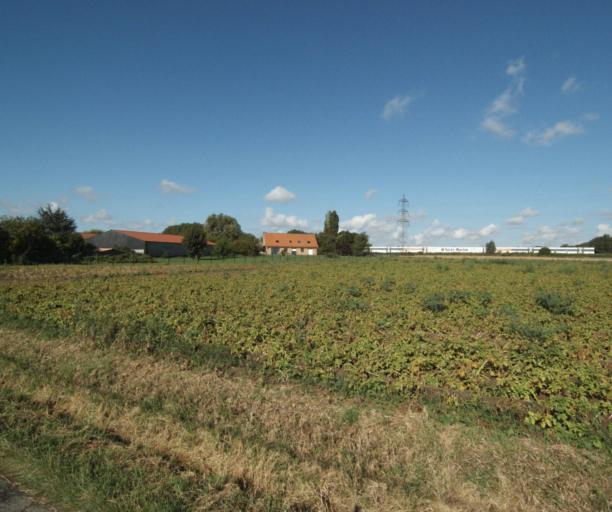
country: FR
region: Nord-Pas-de-Calais
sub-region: Departement du Nord
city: Sailly-lez-Lannoy
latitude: 50.6530
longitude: 3.2120
